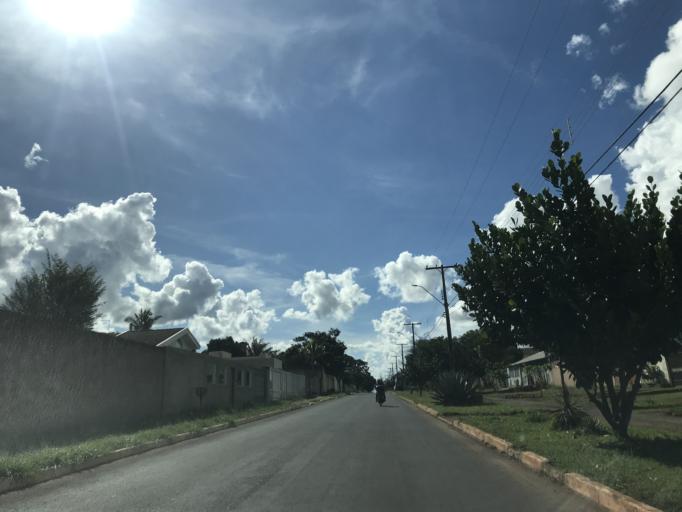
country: BR
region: Federal District
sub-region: Brasilia
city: Brasilia
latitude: -15.7467
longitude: -47.7512
